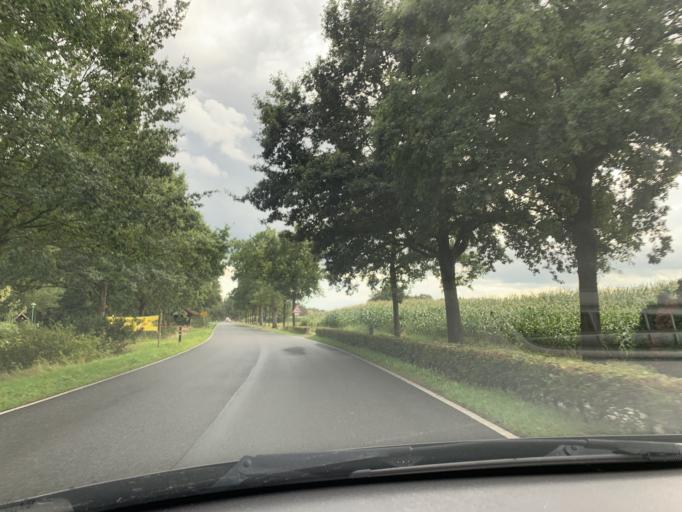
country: DE
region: Lower Saxony
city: Westerstede
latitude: 53.3110
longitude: 7.9168
